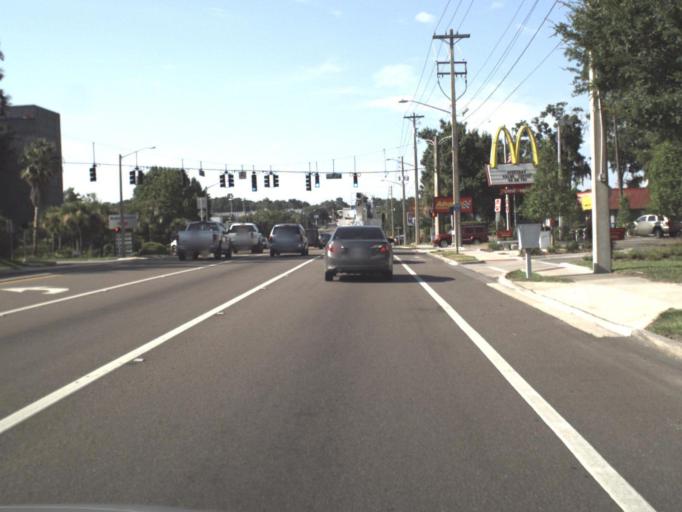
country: US
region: Florida
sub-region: Alachua County
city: Gainesville
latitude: 29.6799
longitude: -82.3392
